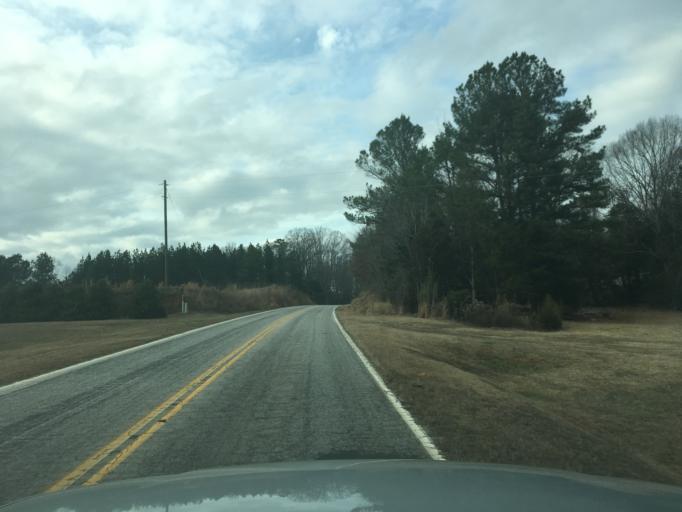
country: US
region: South Carolina
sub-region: Abbeville County
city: Due West
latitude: 34.2903
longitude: -82.4457
